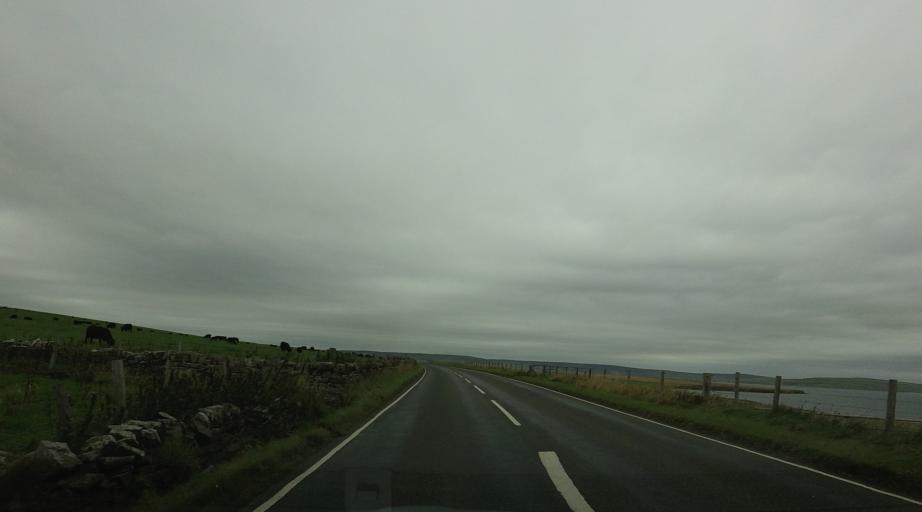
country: GB
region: Scotland
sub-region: Orkney Islands
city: Orkney
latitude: 59.0008
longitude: -2.9955
